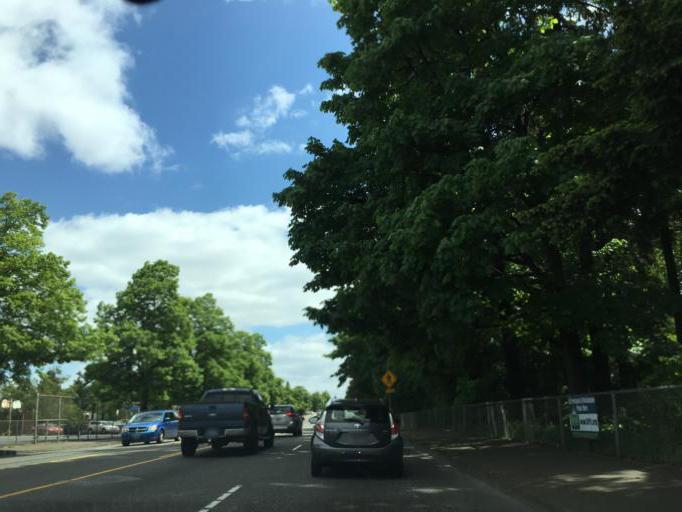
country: US
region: Oregon
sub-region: Multnomah County
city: Lents
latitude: 45.4976
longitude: -122.6181
